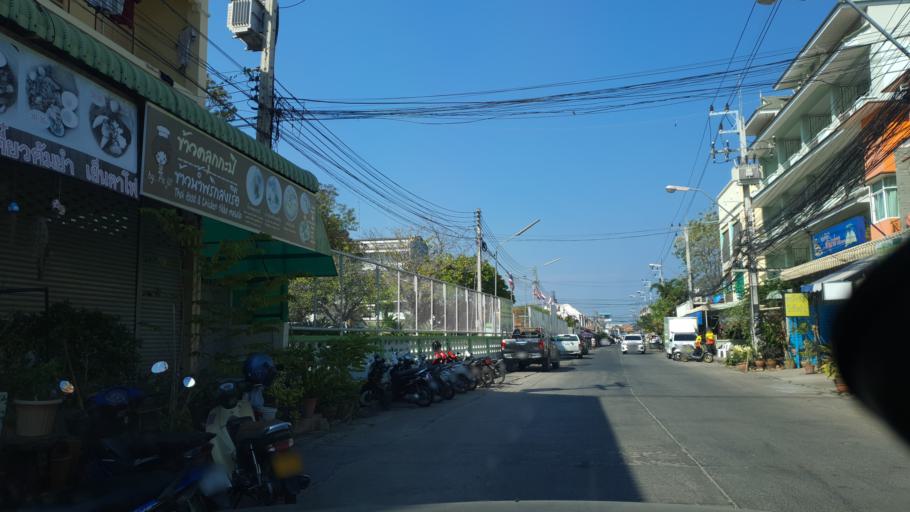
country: TH
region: Prachuap Khiri Khan
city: Hua Hin
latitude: 12.5566
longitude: 99.9527
